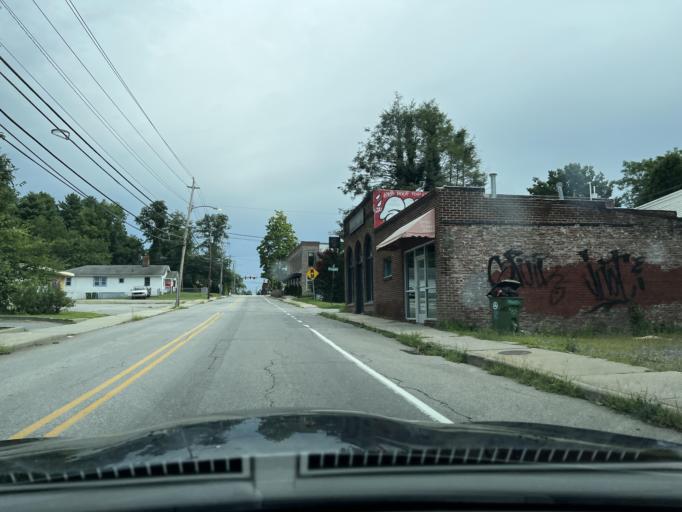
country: US
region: North Carolina
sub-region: Buncombe County
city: Asheville
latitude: 35.5794
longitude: -82.5746
